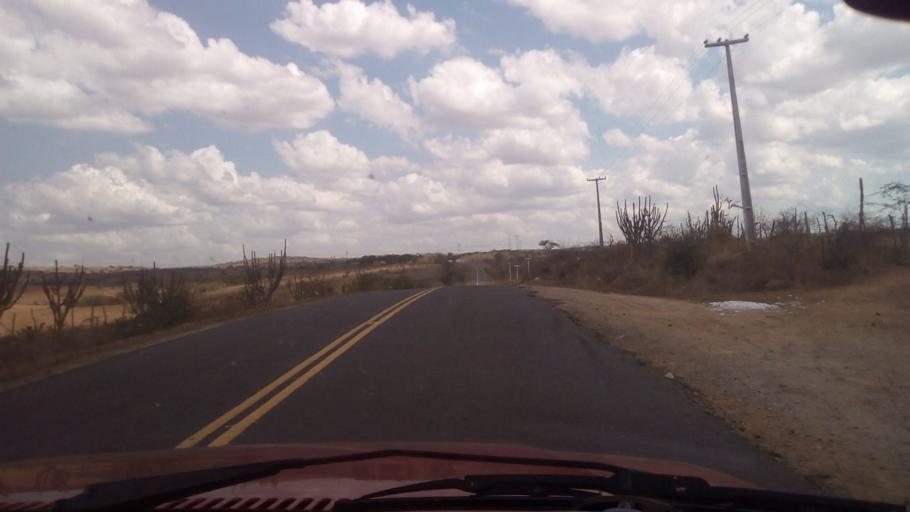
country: BR
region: Paraiba
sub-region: Cacimba De Dentro
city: Cacimba de Dentro
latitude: -6.6936
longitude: -35.7402
